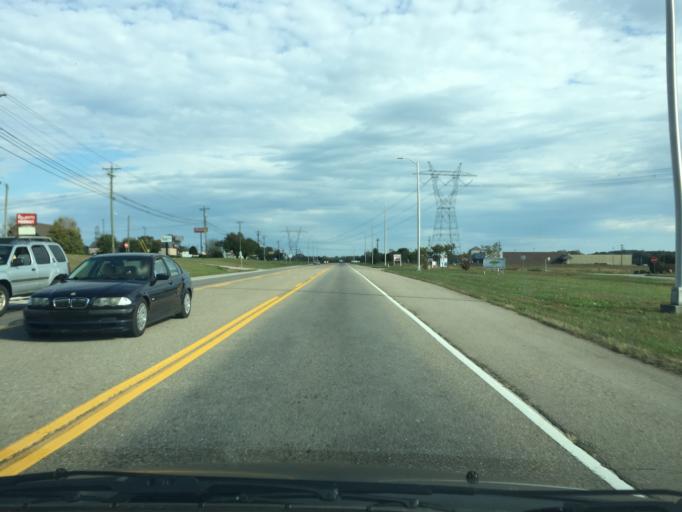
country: US
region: Tennessee
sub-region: Loudon County
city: Loudon
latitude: 35.7203
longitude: -84.3677
